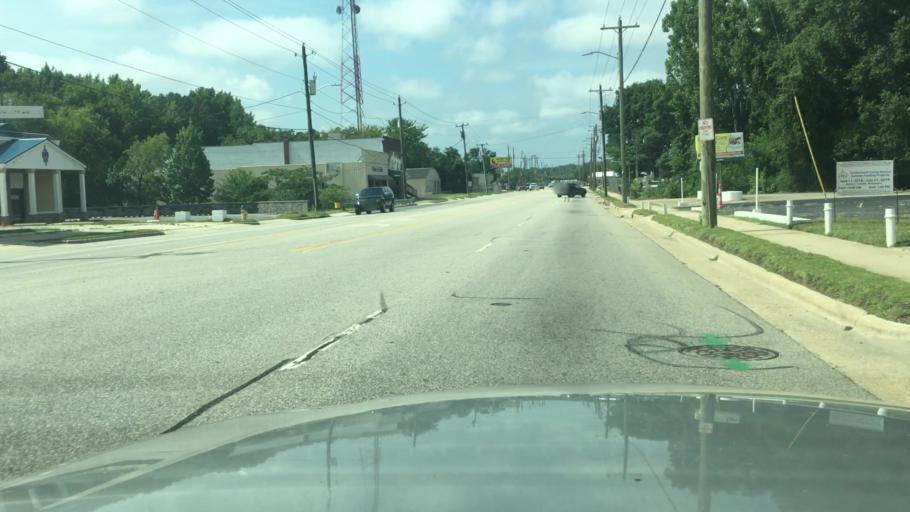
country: US
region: North Carolina
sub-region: Cumberland County
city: Fayetteville
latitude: 35.0445
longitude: -78.8812
